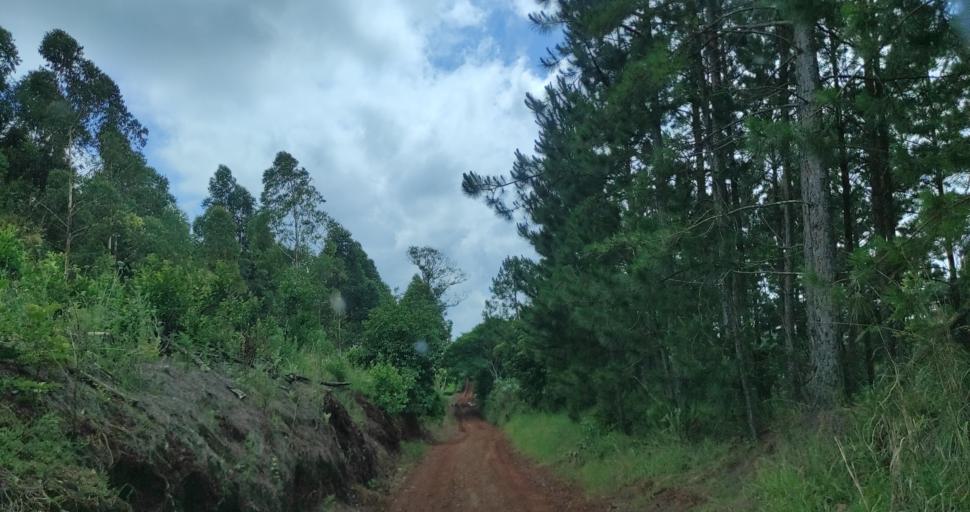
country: AR
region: Misiones
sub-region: Departamento de Veinticinco de Mayo
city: Veinticinco de Mayo
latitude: -27.4187
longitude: -54.7324
